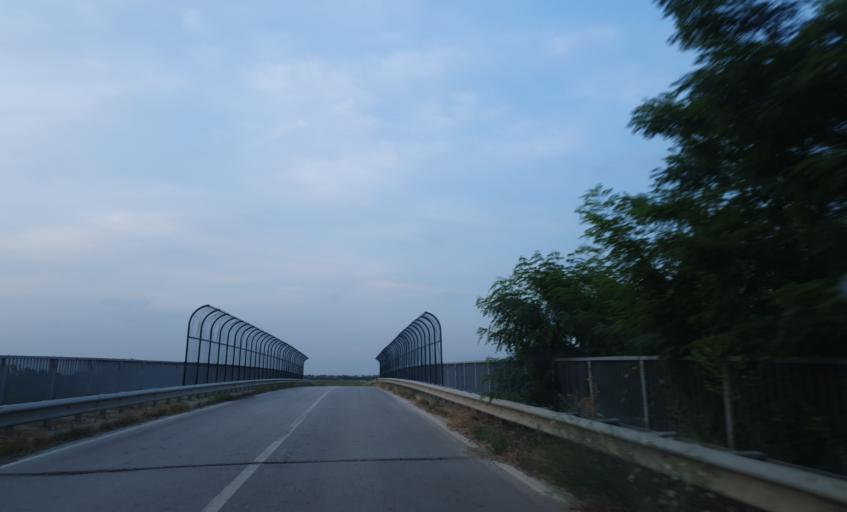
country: TR
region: Kirklareli
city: Buyukkaristiran
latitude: 41.3648
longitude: 27.6079
